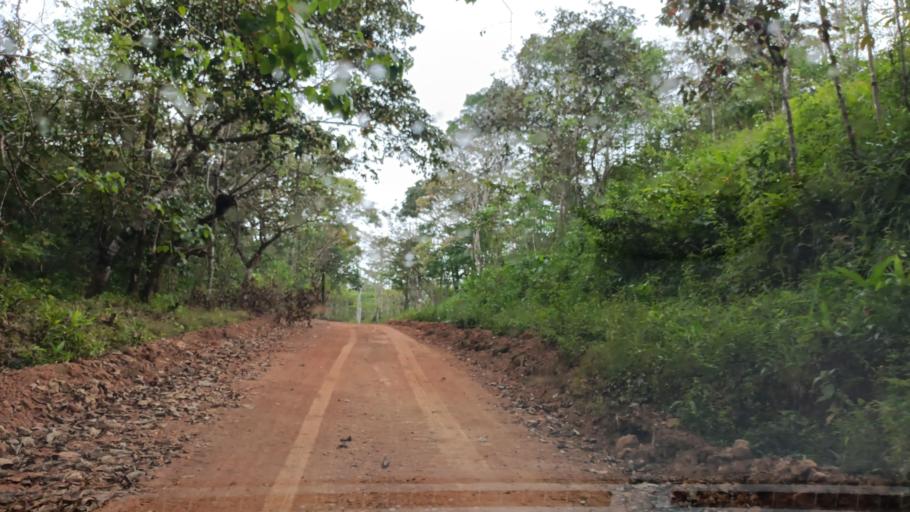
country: PA
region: Panama
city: La Cabima
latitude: 9.1260
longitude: -79.5094
